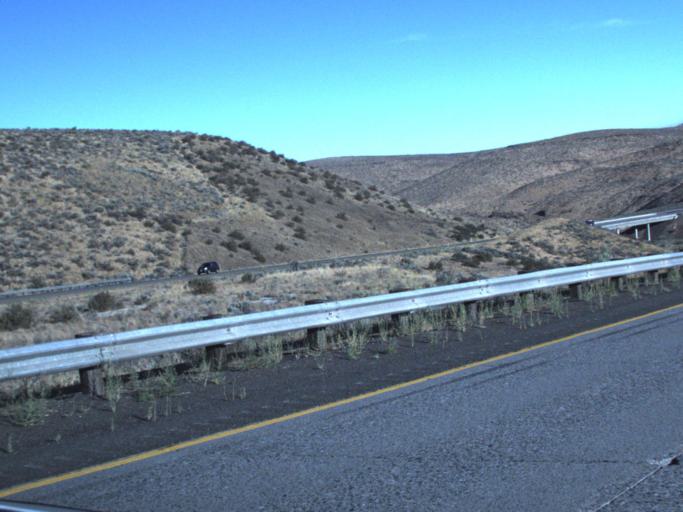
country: US
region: Washington
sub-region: Kittitas County
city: Kittitas
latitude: 46.7962
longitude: -120.3584
